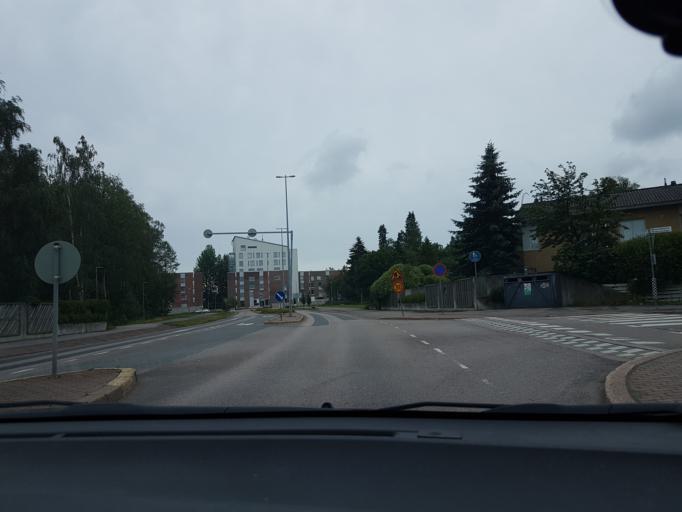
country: FI
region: Uusimaa
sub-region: Helsinki
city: Vantaa
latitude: 60.2801
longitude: 25.0283
